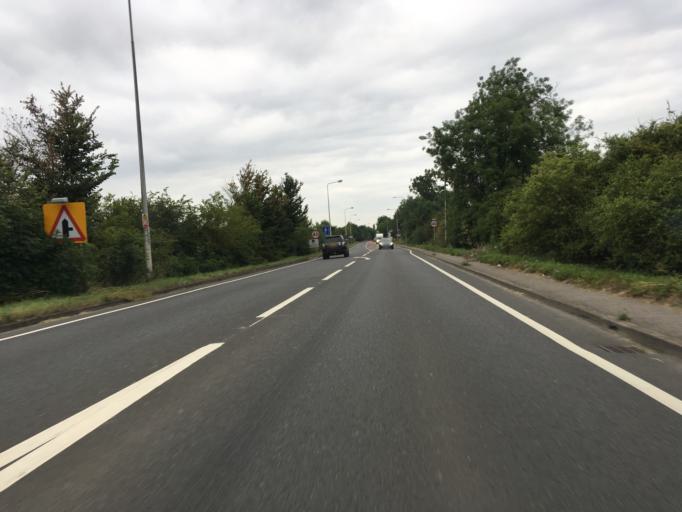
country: GB
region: England
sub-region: Central Bedfordshire
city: Hockliffe
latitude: 51.9224
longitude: -0.5732
